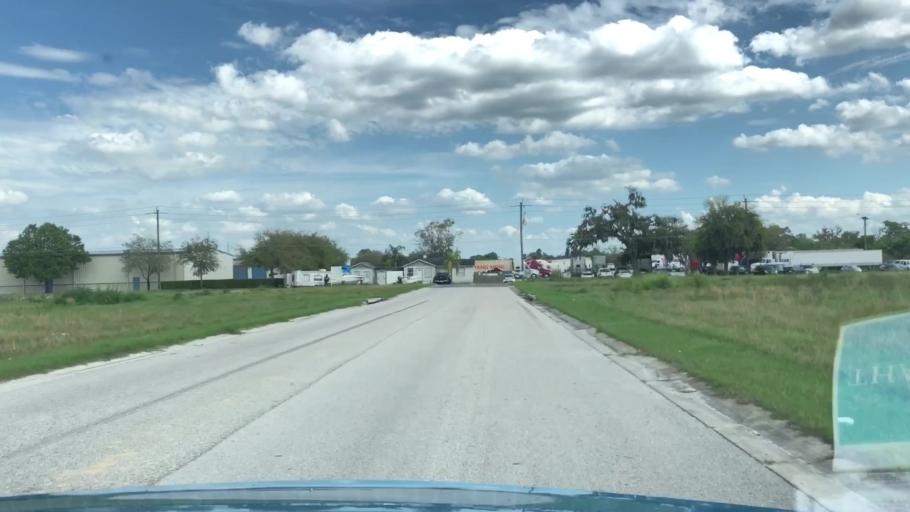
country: US
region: Florida
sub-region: Seminole County
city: Sanford
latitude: 28.8217
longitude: -81.3281
